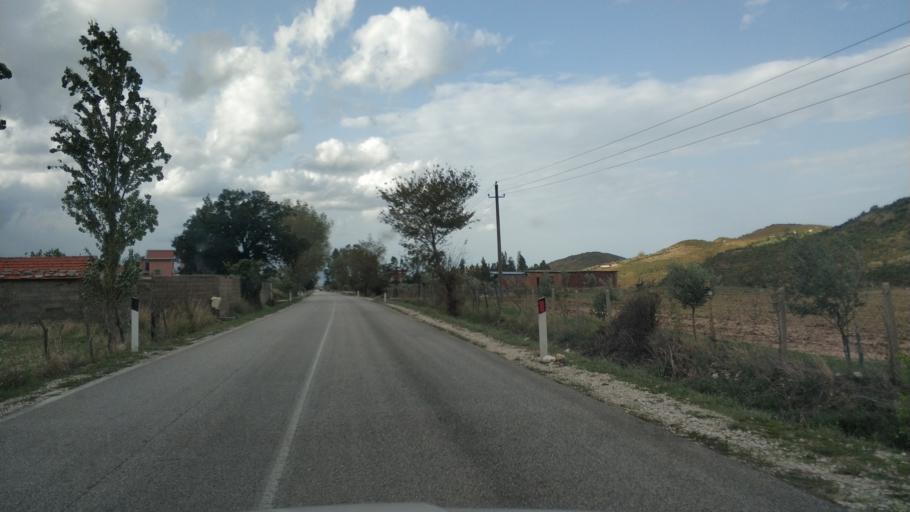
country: AL
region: Vlore
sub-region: Rrethi i Vlores
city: Orikum
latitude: 40.2808
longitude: 19.5019
